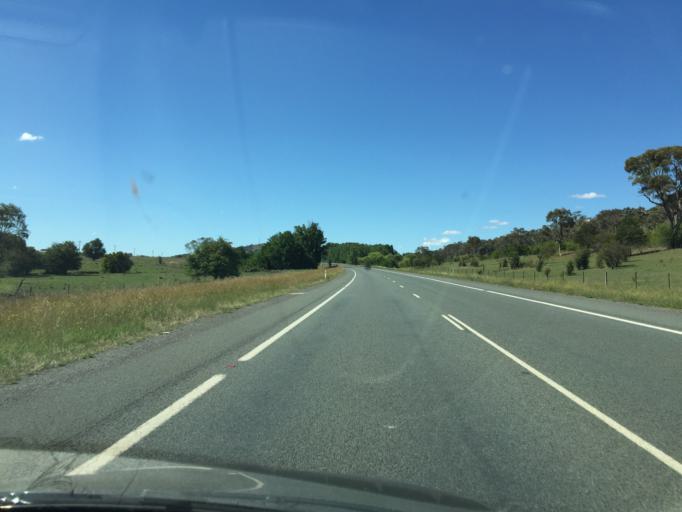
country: AU
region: Australian Capital Territory
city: Macarthur
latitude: -35.4979
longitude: 149.1504
